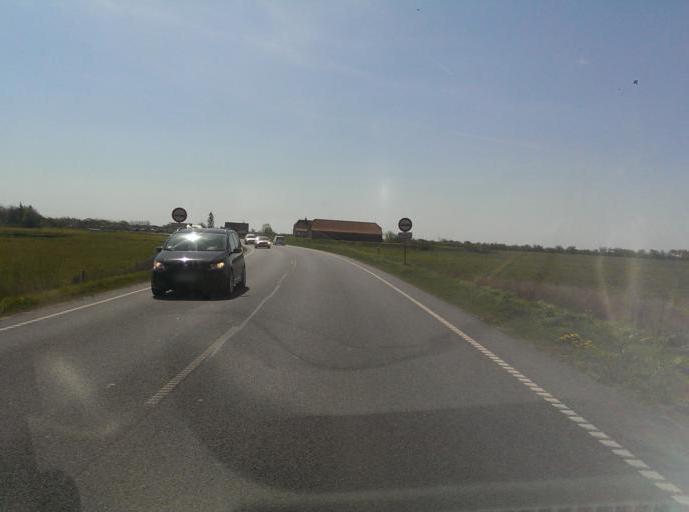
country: DK
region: South Denmark
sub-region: Esbjerg Kommune
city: Ribe
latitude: 55.3308
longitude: 8.7520
